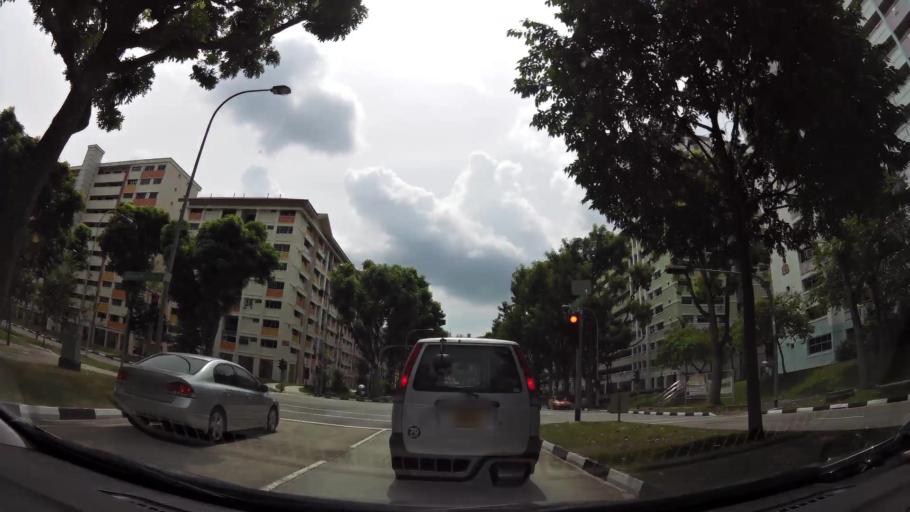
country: MY
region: Johor
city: Johor Bahru
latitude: 1.3470
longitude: 103.6970
